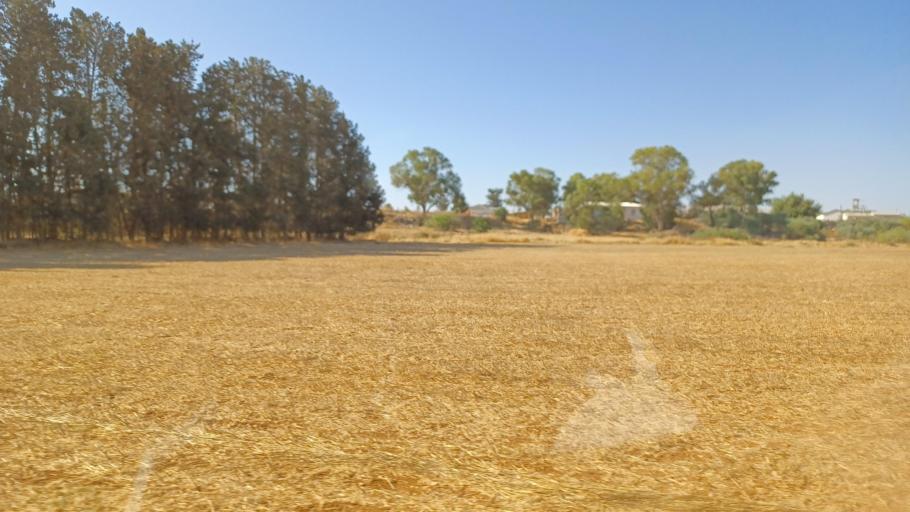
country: CY
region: Larnaka
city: Pergamos
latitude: 35.0497
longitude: 33.7043
